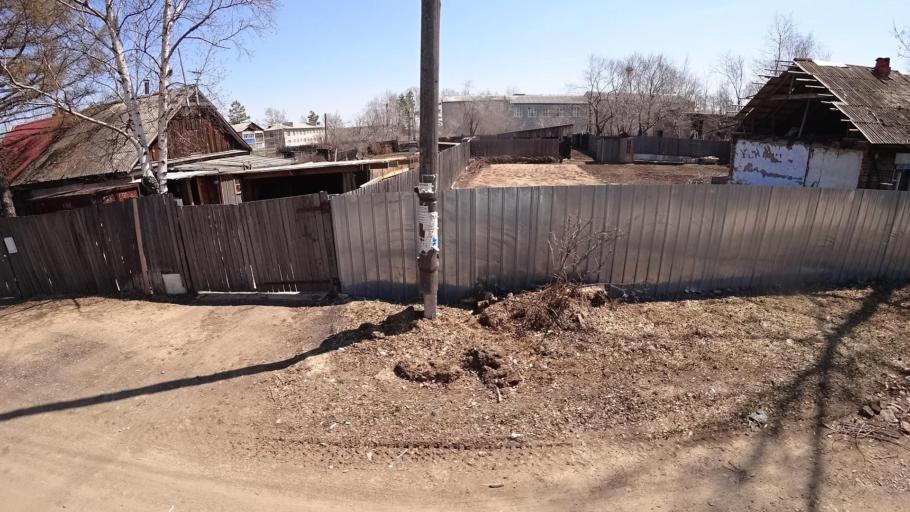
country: RU
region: Khabarovsk Krai
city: Khurba
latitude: 50.4049
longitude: 136.8851
